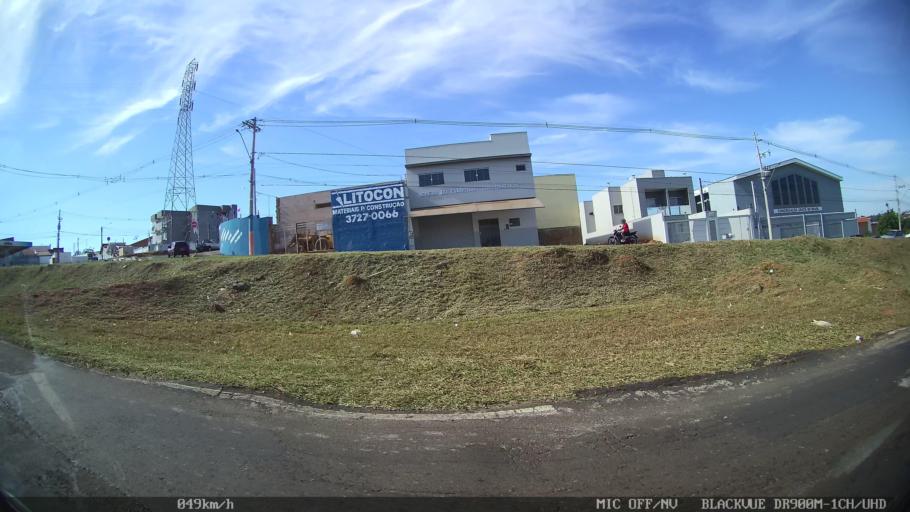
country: BR
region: Sao Paulo
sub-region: Franca
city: Franca
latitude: -20.5155
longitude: -47.4392
